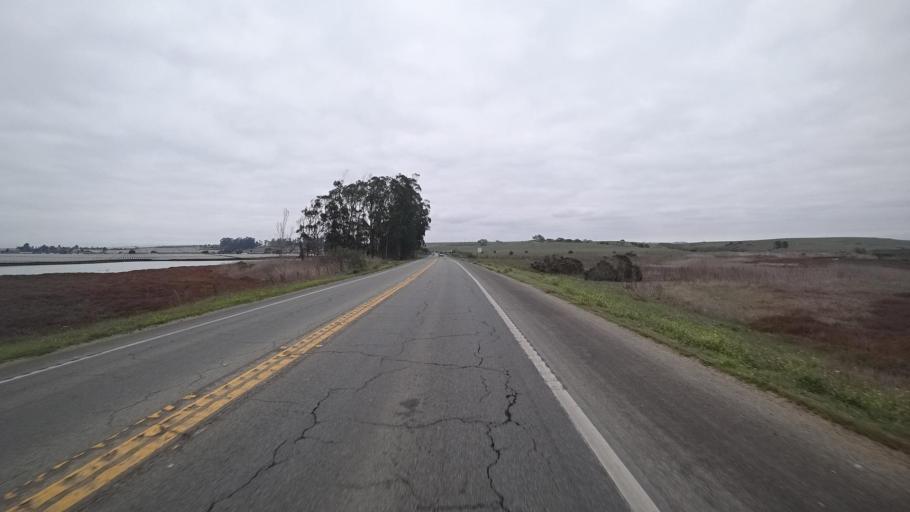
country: US
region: California
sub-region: Monterey County
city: Elkhorn
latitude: 36.8261
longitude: -121.7768
